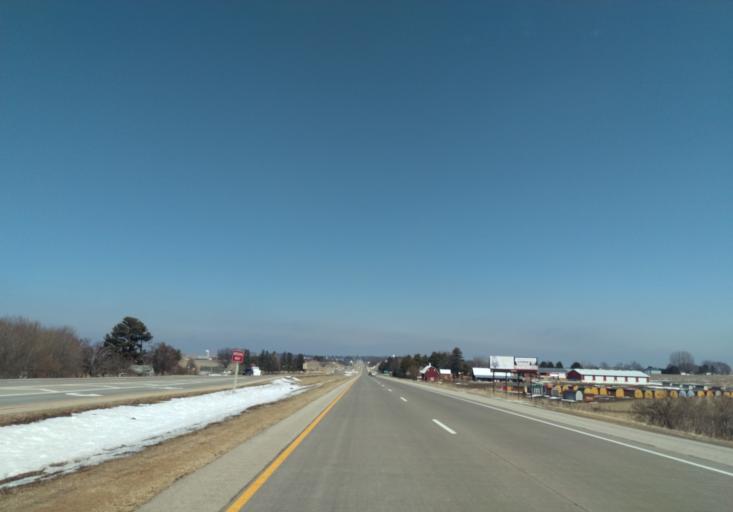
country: US
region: Wisconsin
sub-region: Vernon County
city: Westby
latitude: 43.6206
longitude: -90.8791
